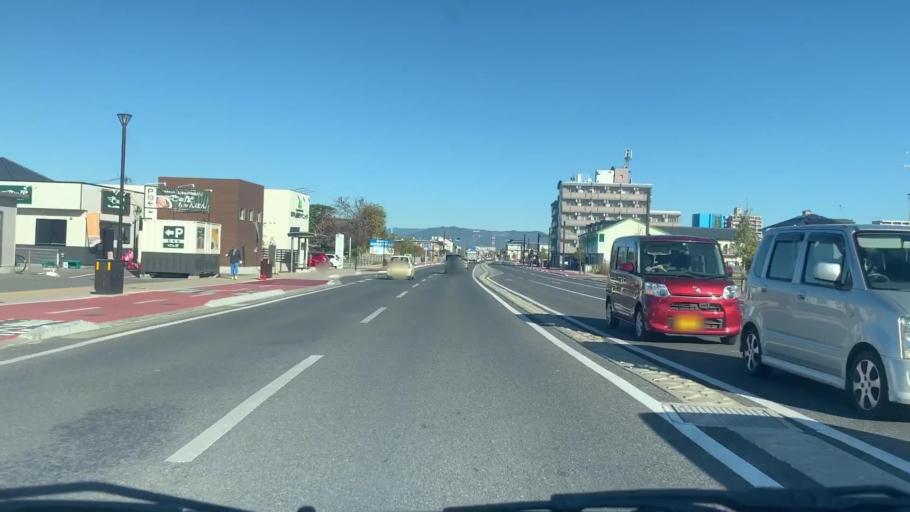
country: JP
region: Saga Prefecture
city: Saga-shi
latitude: 33.2451
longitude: 130.2933
